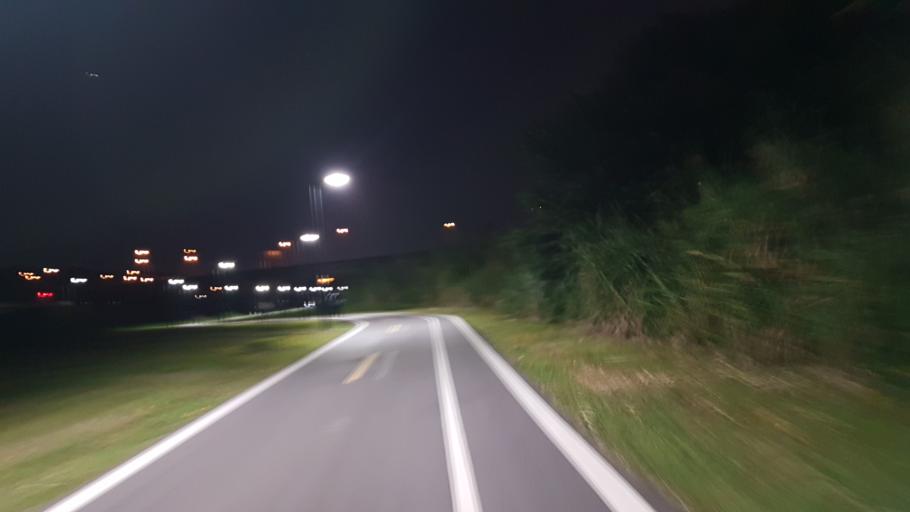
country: TW
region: Taipei
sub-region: Taipei
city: Banqiao
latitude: 24.9688
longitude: 121.5287
